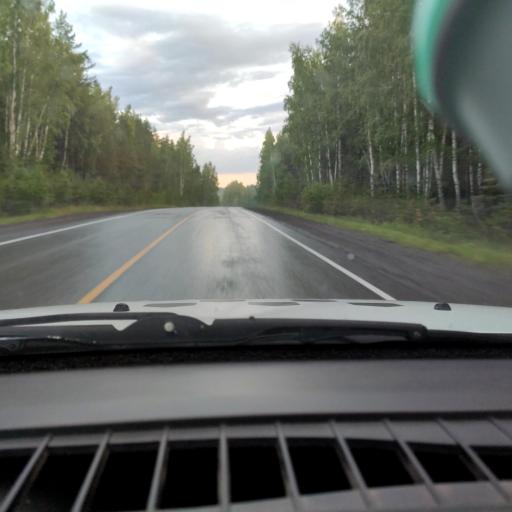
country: RU
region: Chelyabinsk
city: Kyshtym
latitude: 55.7581
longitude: 60.5557
